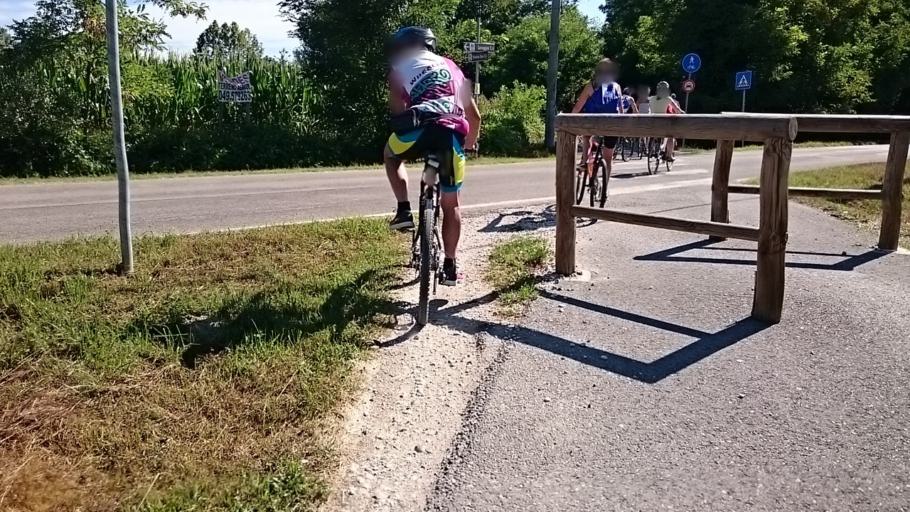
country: IT
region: Veneto
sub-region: Provincia di Padova
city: Loreggia
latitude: 45.5849
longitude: 11.9489
